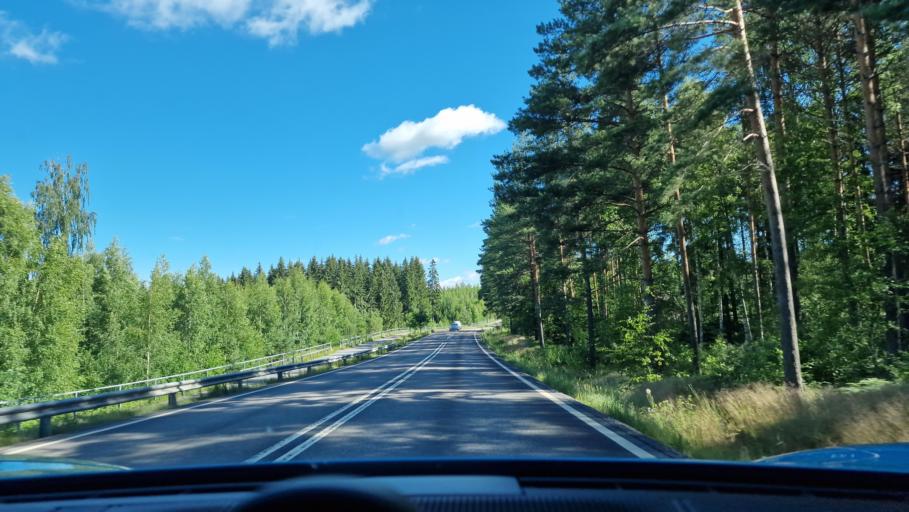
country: FI
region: Pirkanmaa
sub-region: Tampere
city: Kangasala
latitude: 61.4693
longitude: 24.1295
